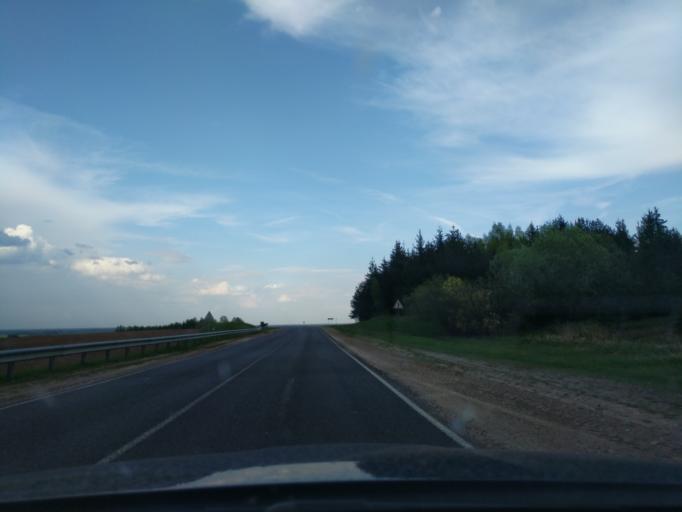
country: BY
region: Grodnenskaya
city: Navahrudak
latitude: 53.6465
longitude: 25.9309
